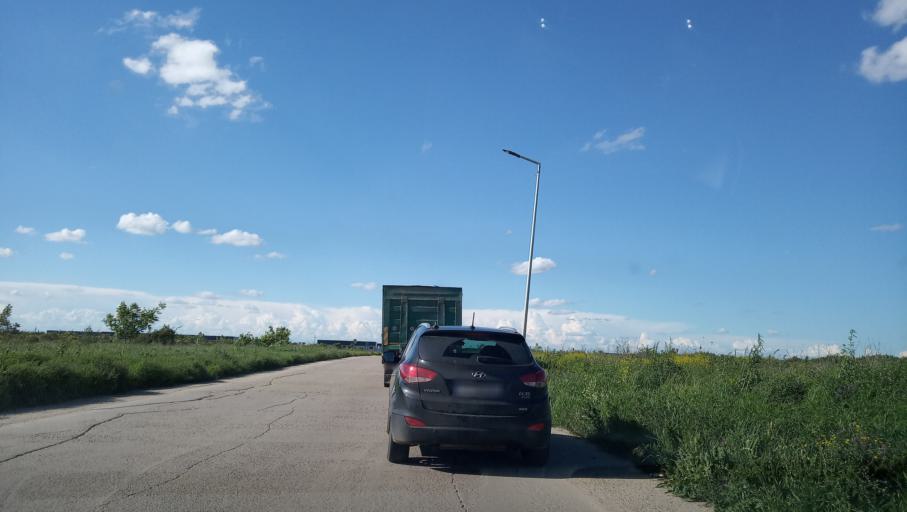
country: RO
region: Ilfov
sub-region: Comuna Chiajna
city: Chiajna
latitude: 44.4475
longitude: 25.9579
